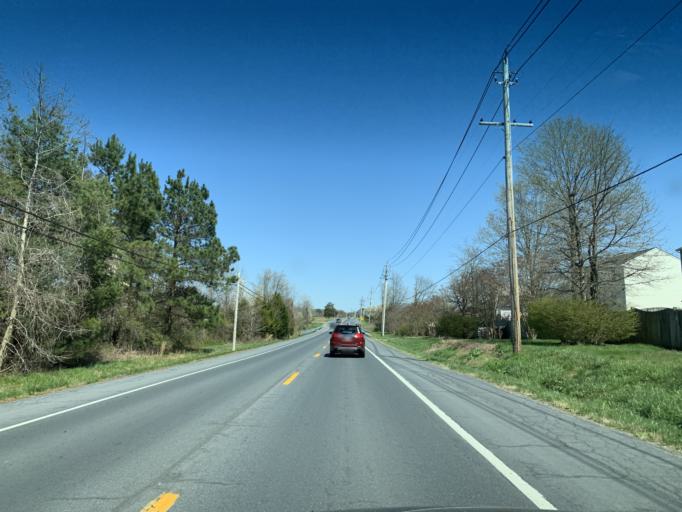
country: US
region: Maryland
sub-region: Talbot County
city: Easton
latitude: 38.7851
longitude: -76.0469
